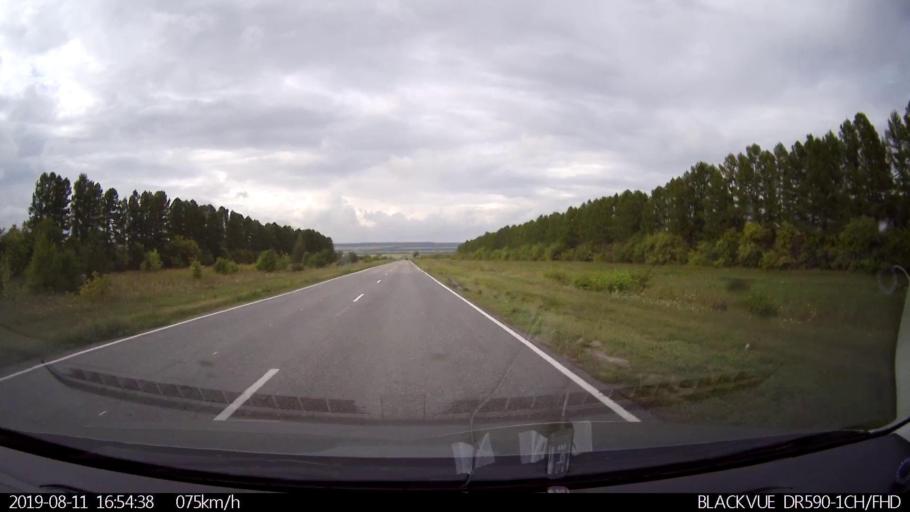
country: RU
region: Ulyanovsk
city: Mayna
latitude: 54.2746
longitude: 47.6659
